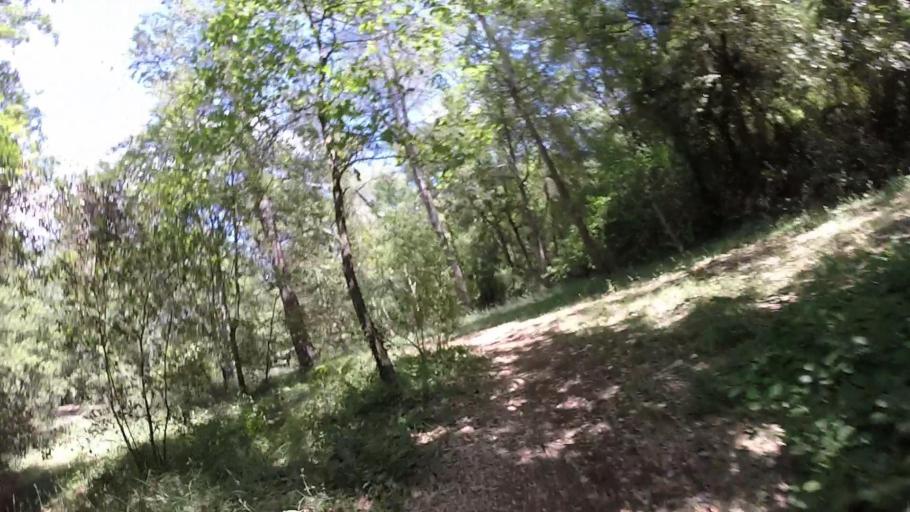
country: FR
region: Provence-Alpes-Cote d'Azur
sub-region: Departement des Alpes-Maritimes
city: Mougins
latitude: 43.6043
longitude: 7.0284
